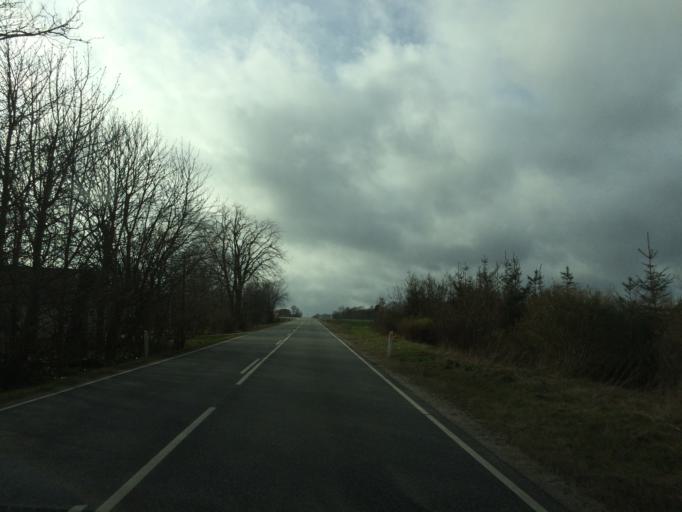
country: DK
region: Central Jutland
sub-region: Favrskov Kommune
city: Ulstrup
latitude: 56.4948
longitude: 9.8420
